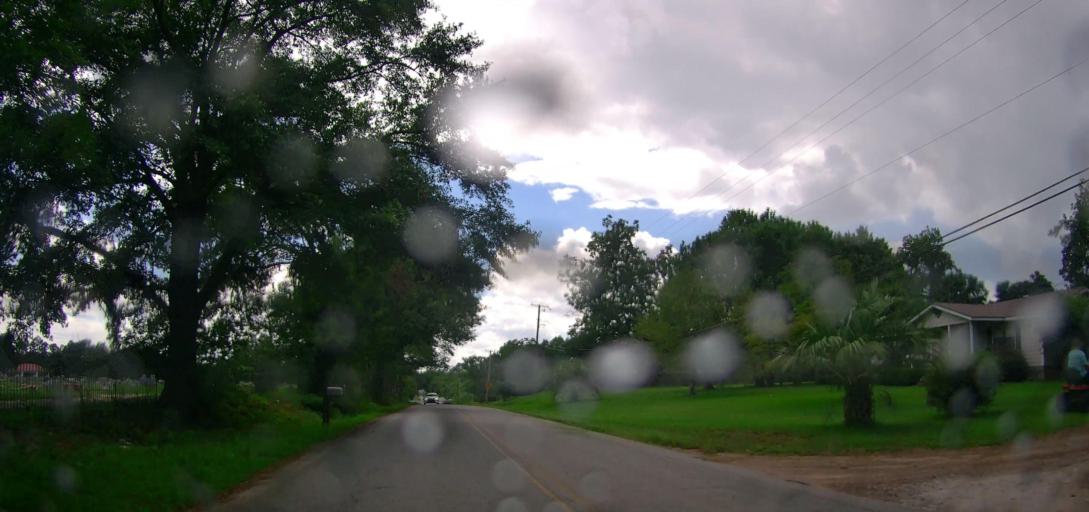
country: US
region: Georgia
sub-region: Ben Hill County
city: Fitzgerald
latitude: 31.7067
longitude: -83.2344
